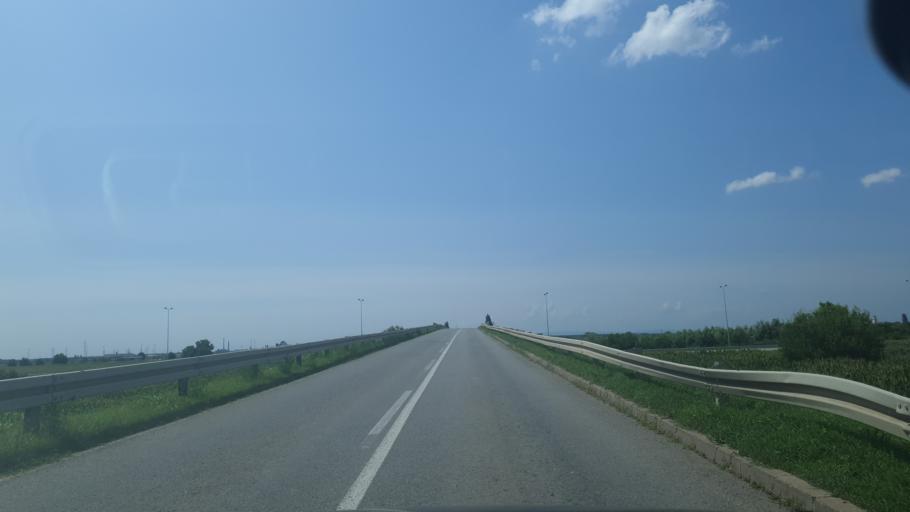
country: RS
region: Autonomna Pokrajina Vojvodina
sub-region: Sremski Okrug
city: Sremska Mitrovica
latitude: 45.0007
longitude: 19.6424
